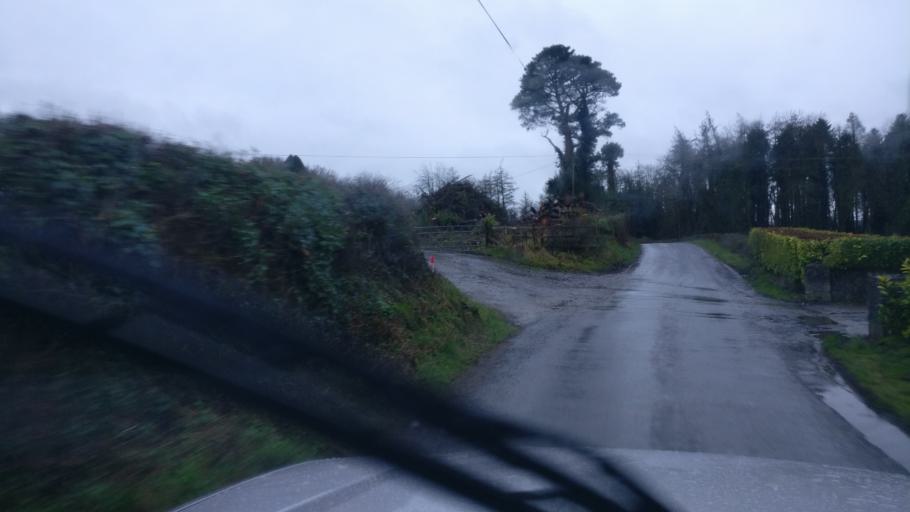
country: IE
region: Connaught
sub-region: County Galway
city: Ballinasloe
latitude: 53.2780
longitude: -8.3057
